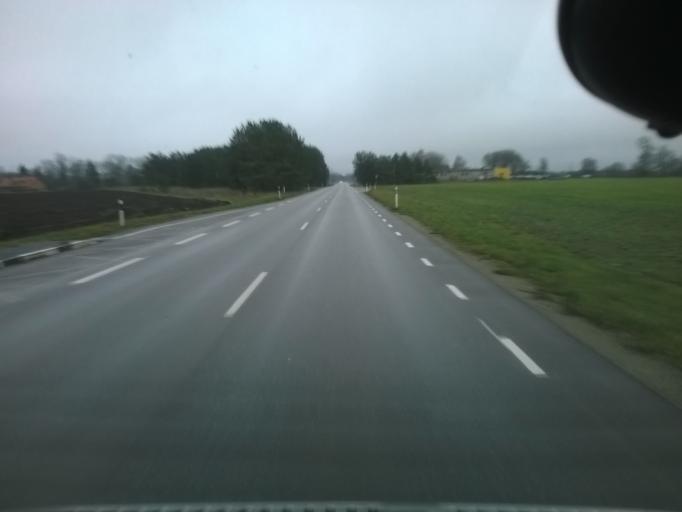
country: EE
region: Harju
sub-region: Saku vald
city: Saku
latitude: 59.2673
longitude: 24.7297
